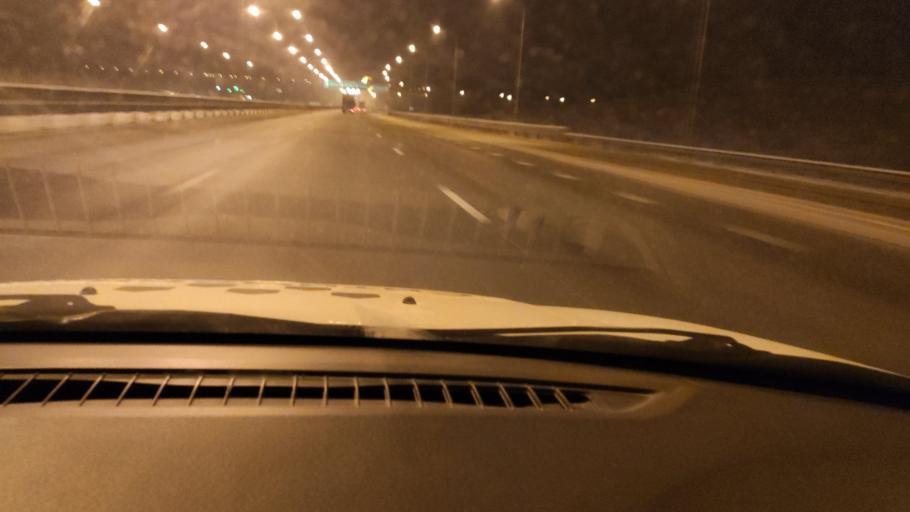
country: RU
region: Perm
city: Lobanovo
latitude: 57.7989
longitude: 56.3286
